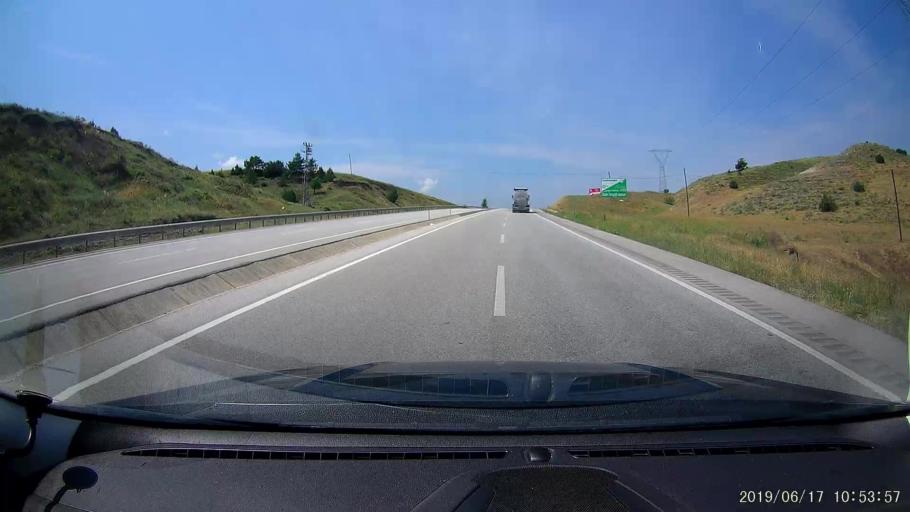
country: TR
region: Corum
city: Hacihamza
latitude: 41.0767
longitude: 34.3108
